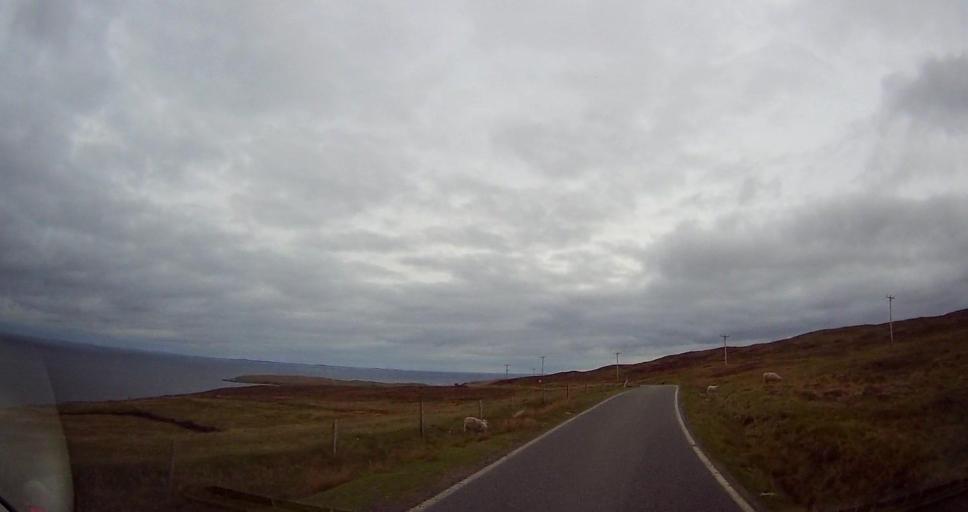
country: GB
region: Scotland
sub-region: Shetland Islands
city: Shetland
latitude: 60.5451
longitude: -1.0556
